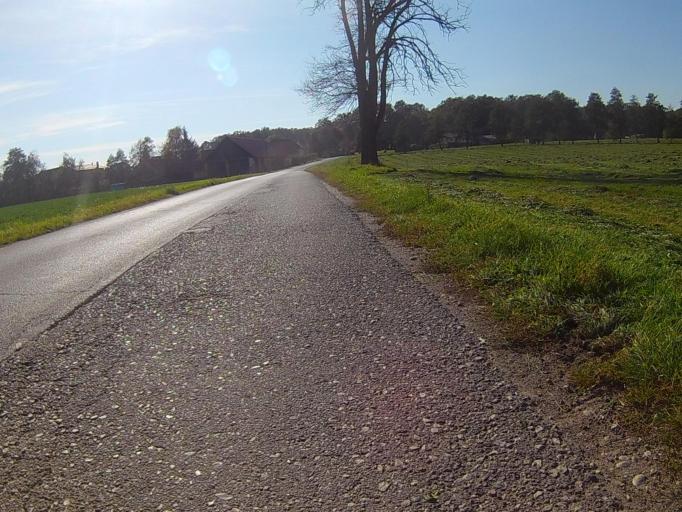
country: SI
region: Ptuj
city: Ptuj
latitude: 46.4414
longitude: 15.9003
